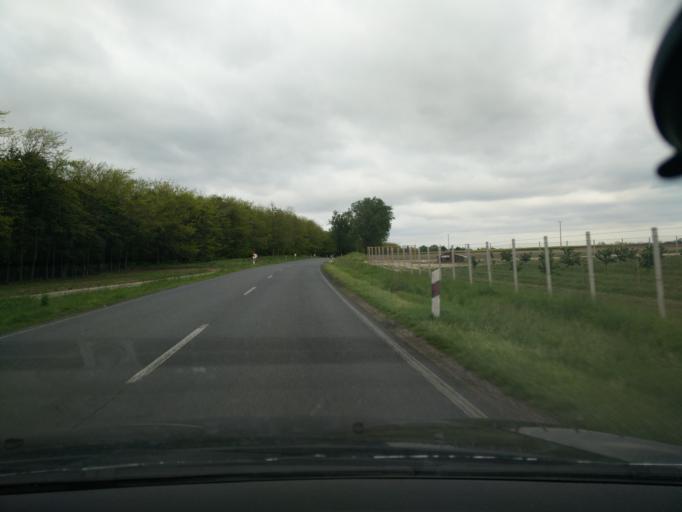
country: HU
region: Veszprem
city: Papa
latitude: 47.3840
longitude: 17.4679
